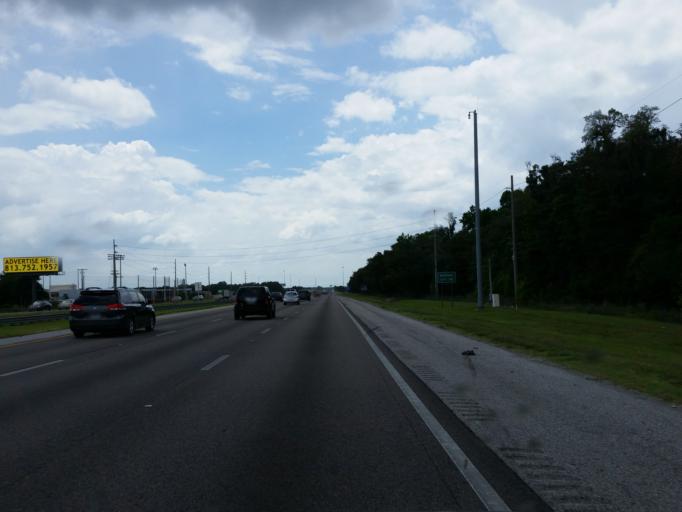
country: US
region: Florida
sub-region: Hillsborough County
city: Dover
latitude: 28.0261
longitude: -82.2304
